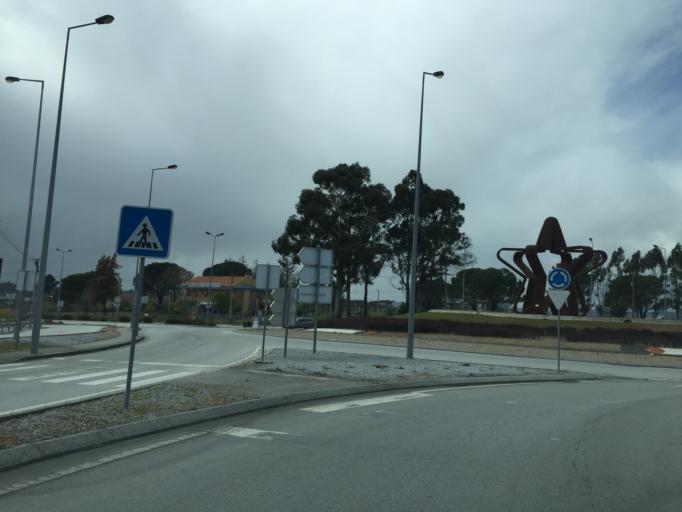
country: PT
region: Guarda
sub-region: Seia
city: Seia
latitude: 40.5120
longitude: -7.6319
